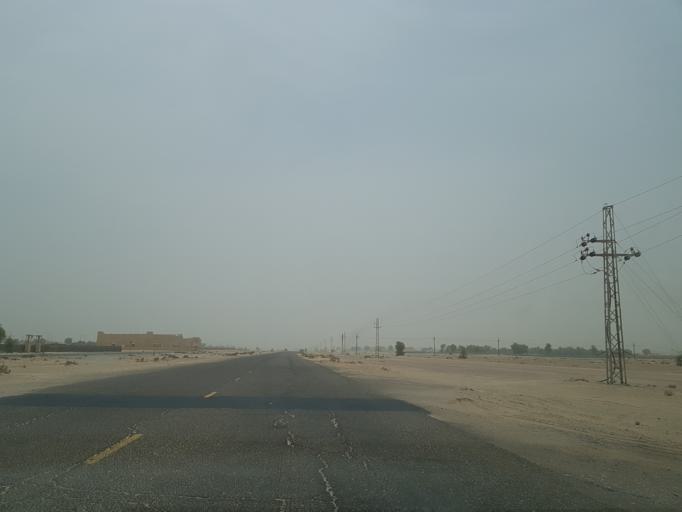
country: AE
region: Dubai
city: Dubai
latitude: 24.9366
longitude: 55.4734
